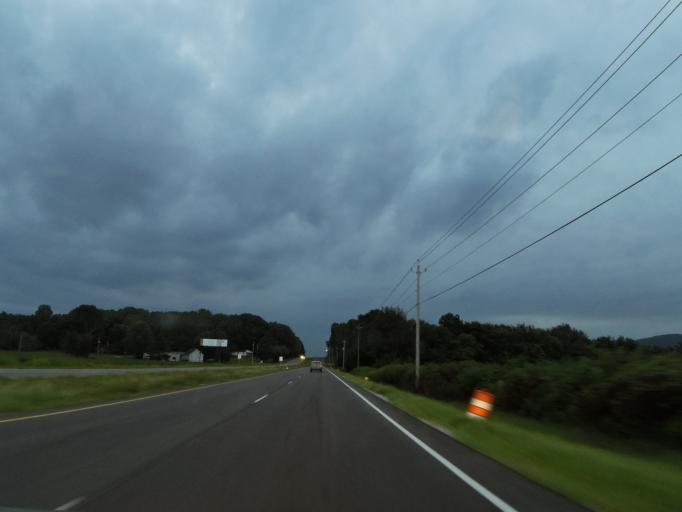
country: US
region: Alabama
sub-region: Madison County
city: Moores Mill
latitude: 34.7652
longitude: -86.4869
